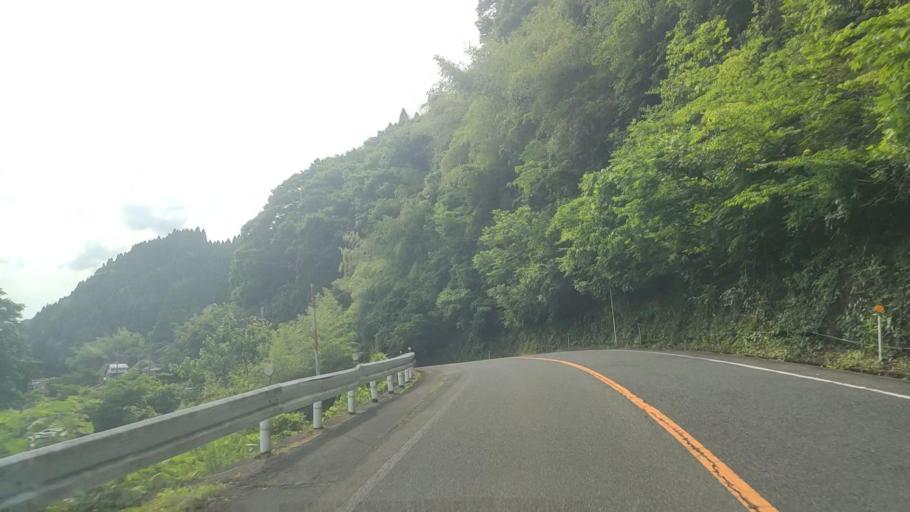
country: JP
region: Tottori
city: Tottori
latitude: 35.3334
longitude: 134.1292
